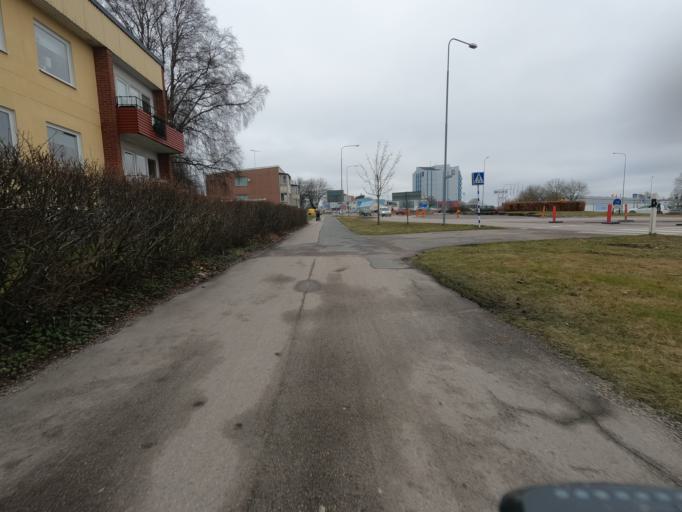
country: SE
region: Kronoberg
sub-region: Ljungby Kommun
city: Ljungby
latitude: 56.8314
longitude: 13.9297
